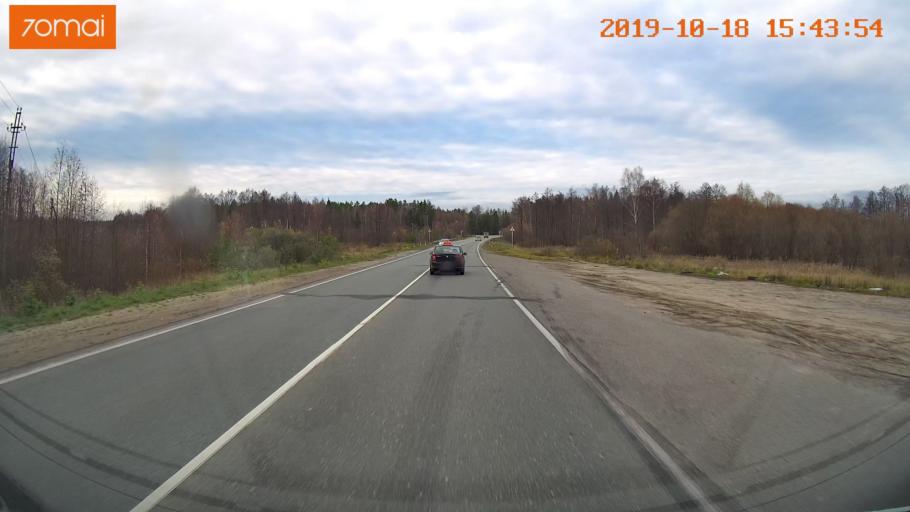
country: RU
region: Vladimir
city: Golovino
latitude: 55.9743
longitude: 40.5473
